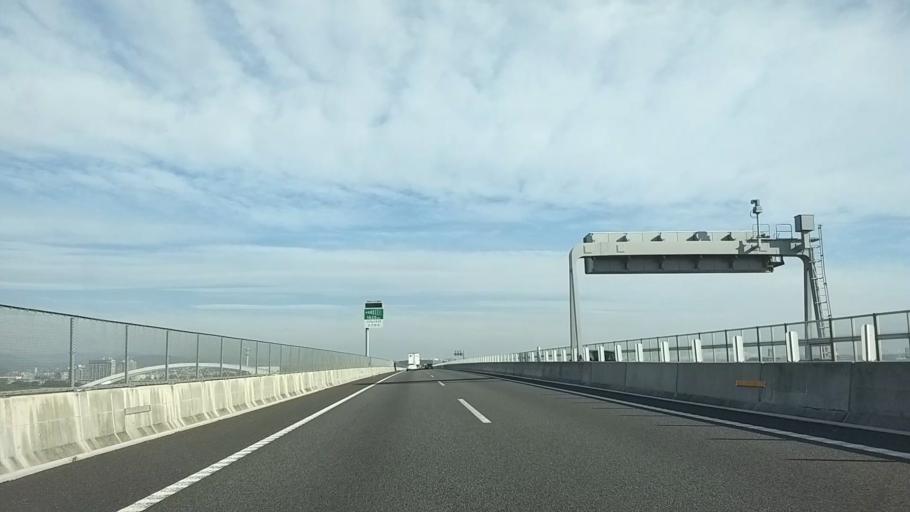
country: JP
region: Kanagawa
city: Atsugi
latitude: 35.4428
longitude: 139.3755
